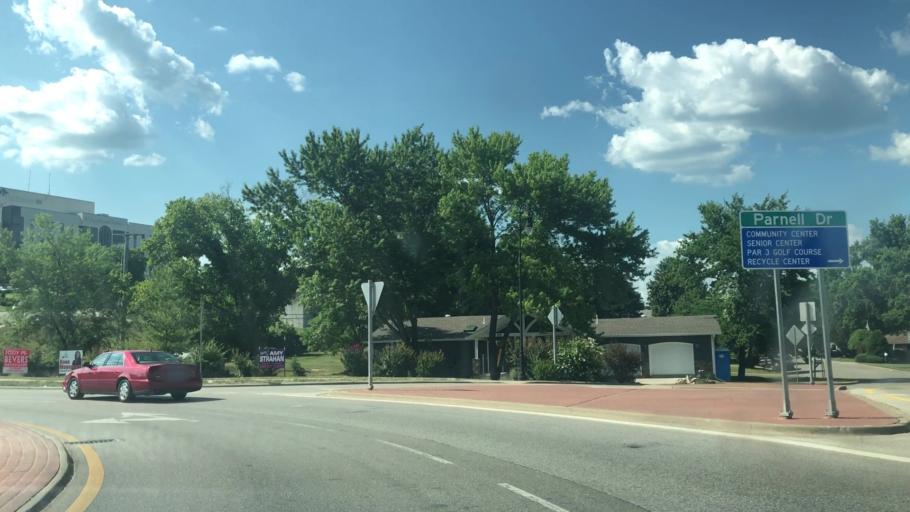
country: US
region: Missouri
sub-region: Taney County
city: Branson
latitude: 36.6499
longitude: -93.2193
